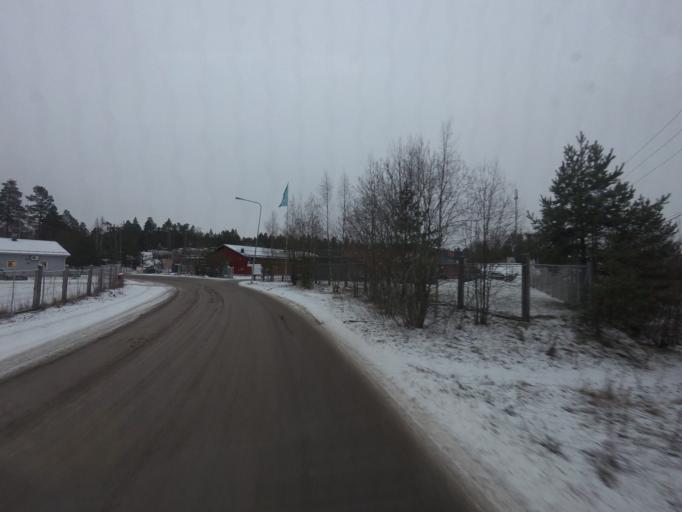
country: FI
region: Uusimaa
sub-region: Helsinki
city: Espoo
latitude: 60.2058
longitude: 24.6245
